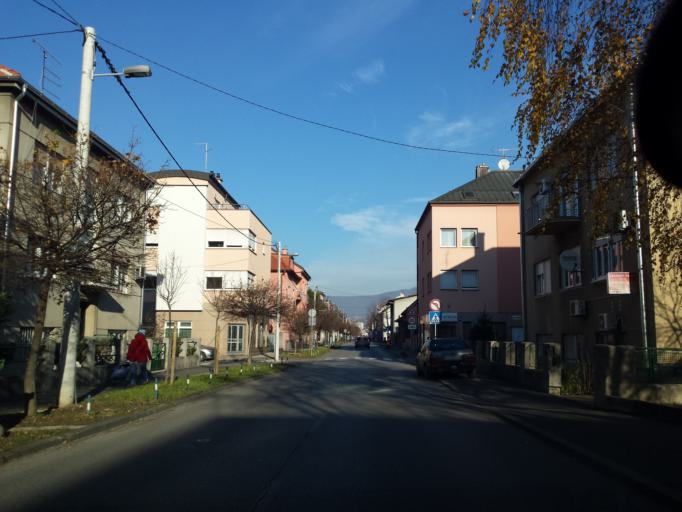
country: HR
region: Grad Zagreb
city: Jankomir
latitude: 45.7979
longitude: 15.9396
